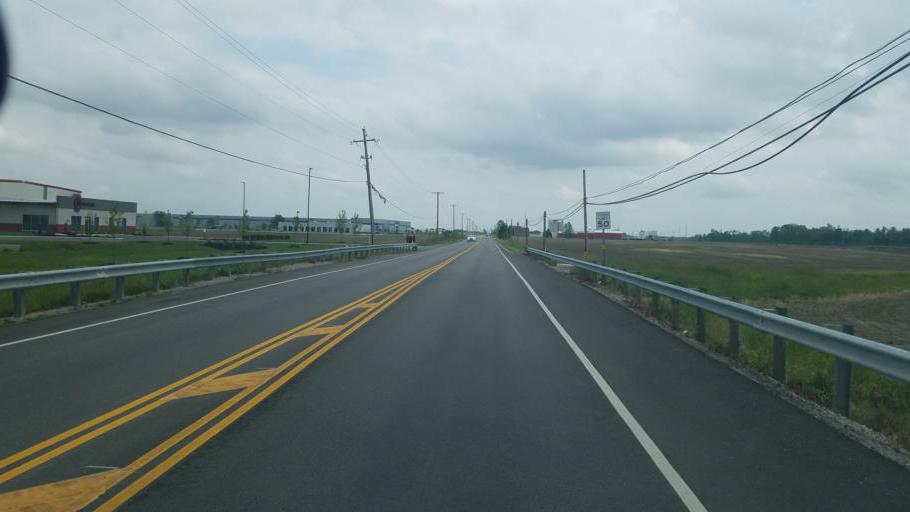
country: US
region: Ohio
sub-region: Union County
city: Marysville
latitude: 40.2235
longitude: -83.3384
